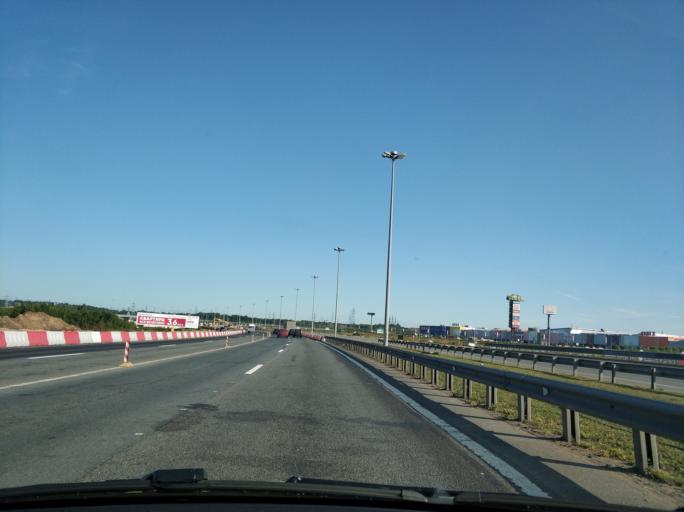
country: RU
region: Leningrad
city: Bugry
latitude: 60.0848
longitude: 30.3778
